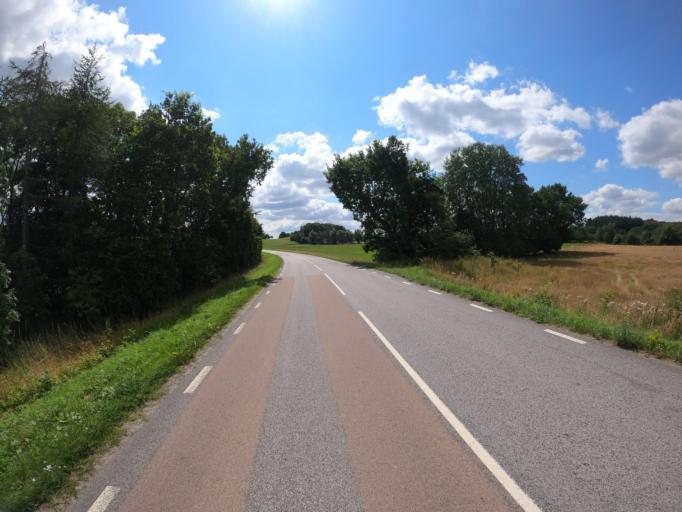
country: SE
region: Skane
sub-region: Lunds Kommun
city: Veberod
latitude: 55.6082
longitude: 13.4878
